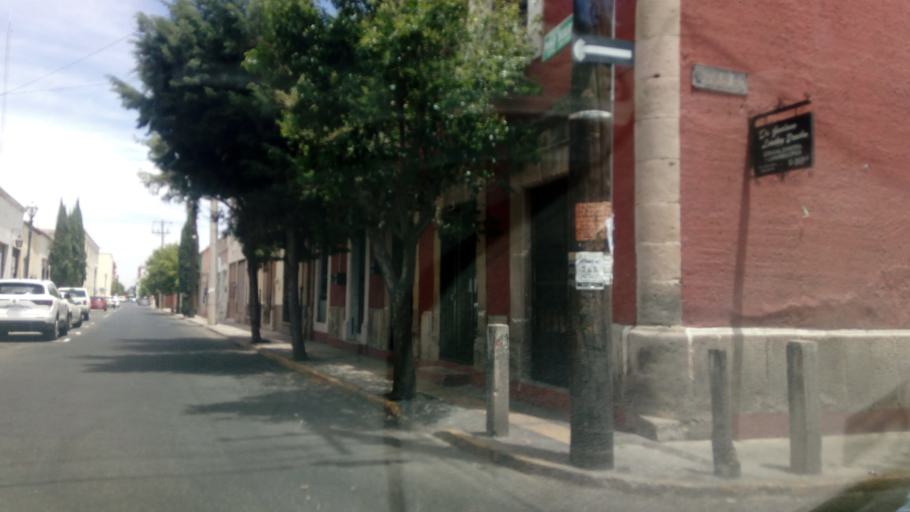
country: MX
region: Durango
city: Victoria de Durango
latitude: 24.0216
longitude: -104.6733
